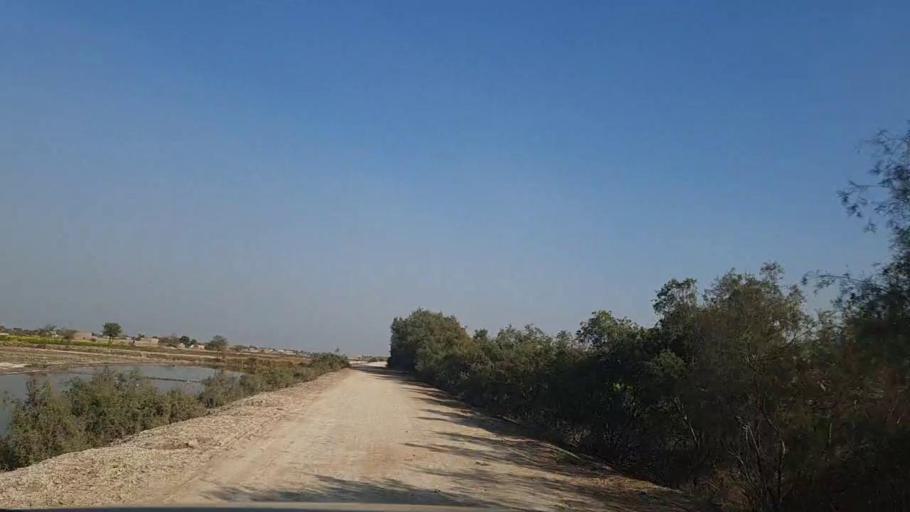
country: PK
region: Sindh
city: Daur
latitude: 26.3178
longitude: 68.1822
